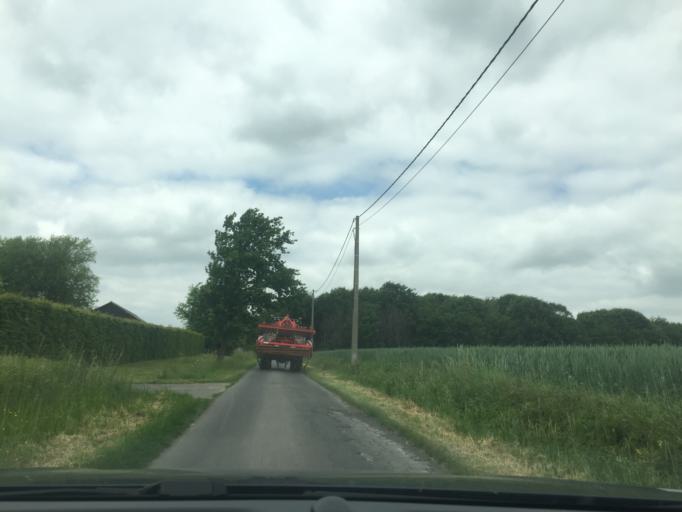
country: BE
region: Wallonia
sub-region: Province du Hainaut
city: Pecq
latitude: 50.6790
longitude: 3.3910
